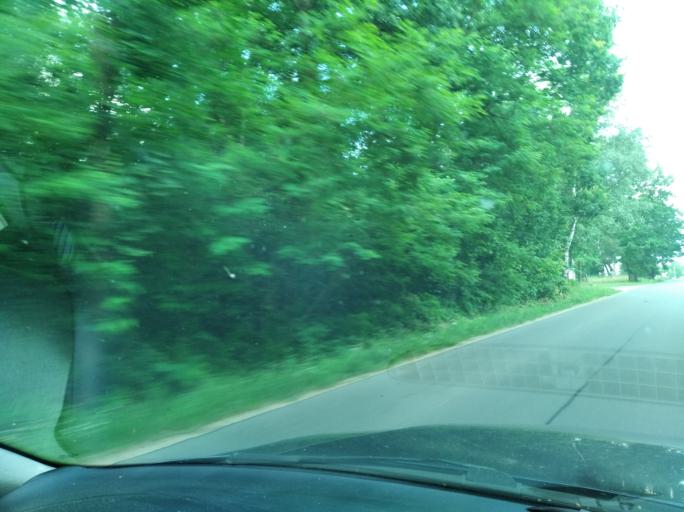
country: PL
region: Subcarpathian Voivodeship
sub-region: Powiat rzeszowski
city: Wysoka Glogowska
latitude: 50.1303
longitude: 22.0240
